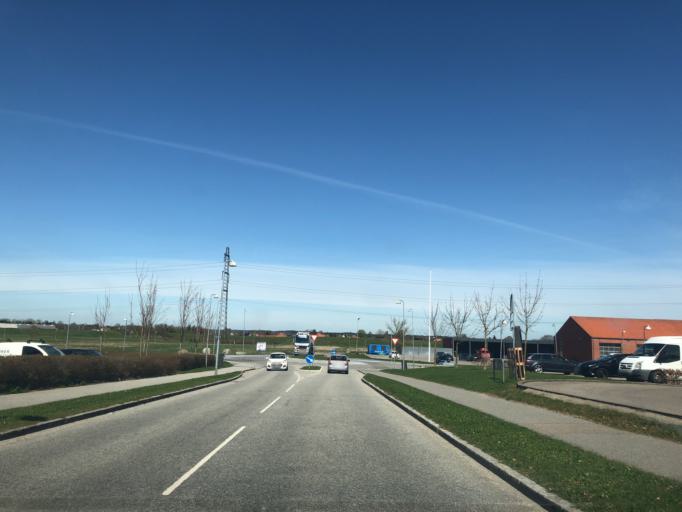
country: DK
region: Zealand
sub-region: Ringsted Kommune
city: Ringsted
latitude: 55.4525
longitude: 11.7843
